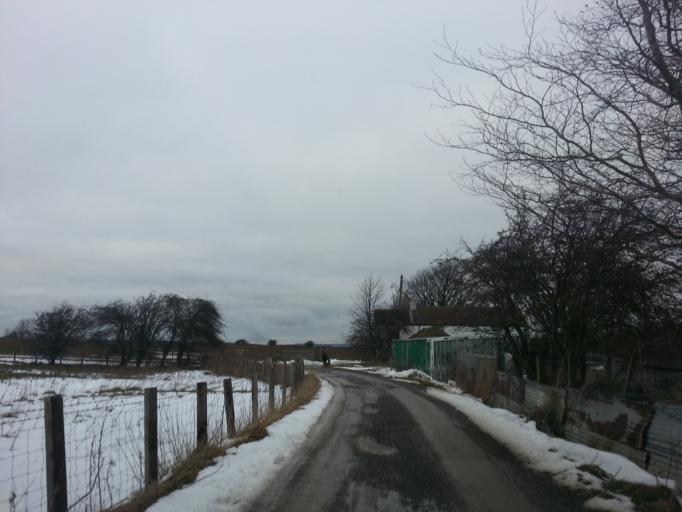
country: GB
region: England
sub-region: County Durham
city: Tow Law
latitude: 54.7731
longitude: -1.7934
